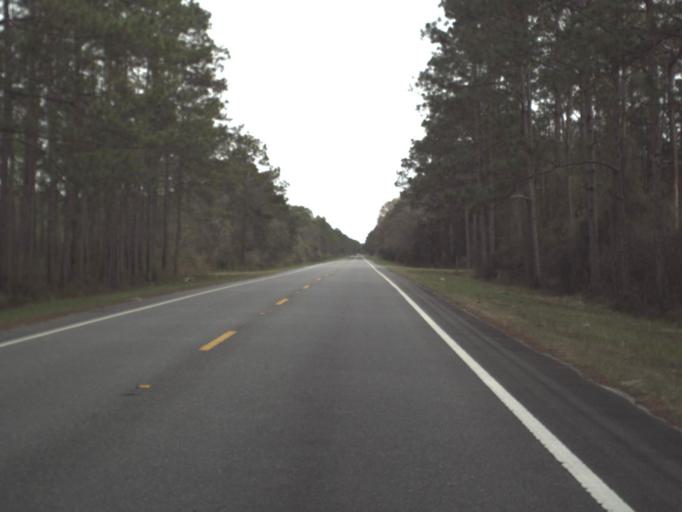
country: US
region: Florida
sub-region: Gadsden County
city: Midway
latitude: 30.3326
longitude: -84.4742
